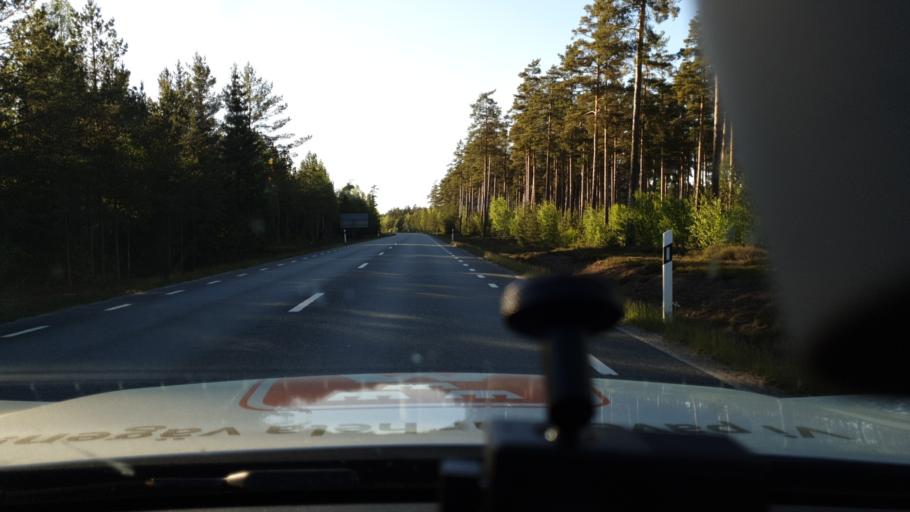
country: SE
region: Joenkoeping
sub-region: Eksjo Kommun
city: Eksjoe
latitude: 57.6385
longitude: 14.9649
